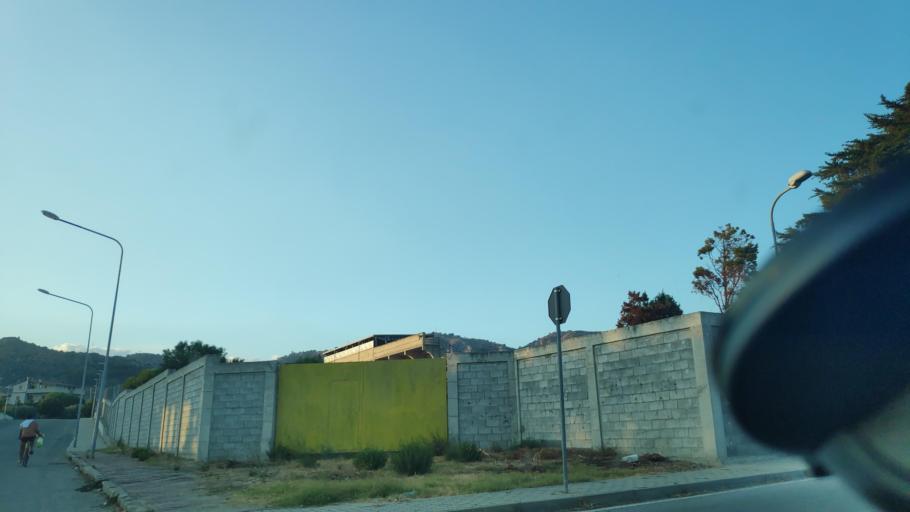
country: IT
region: Calabria
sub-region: Provincia di Reggio Calabria
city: Roccella Ionica
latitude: 38.3207
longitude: 16.3936
